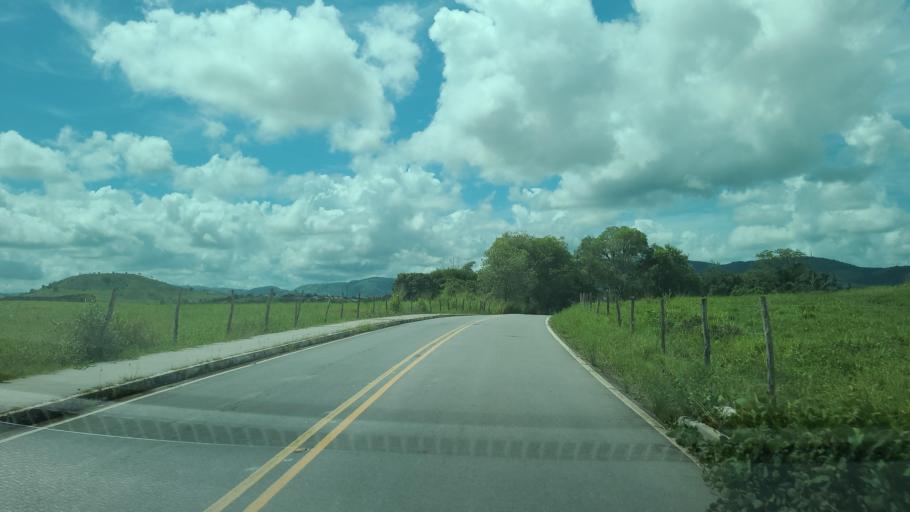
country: BR
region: Alagoas
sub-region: Uniao Dos Palmares
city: Uniao dos Palmares
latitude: -9.1629
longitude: -36.0508
